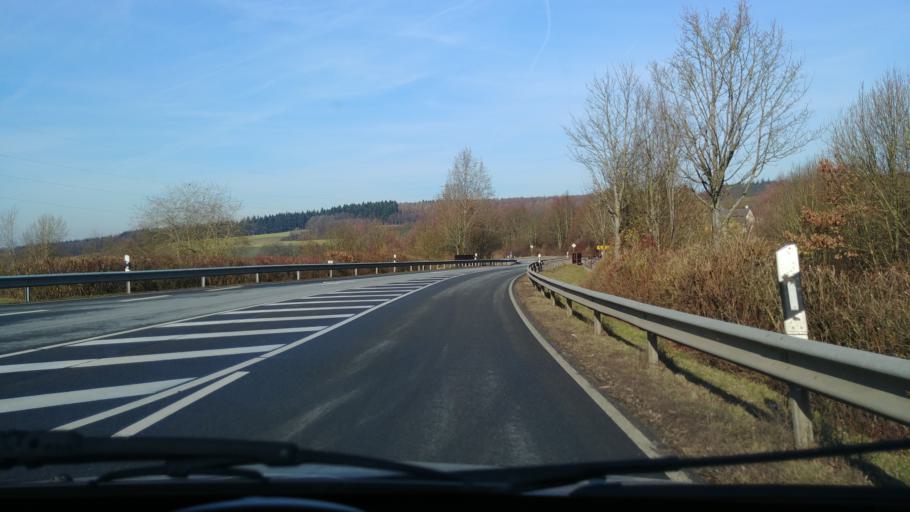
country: DE
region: Rheinland-Pfalz
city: Dachsenhausen
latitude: 50.2521
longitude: 7.7224
